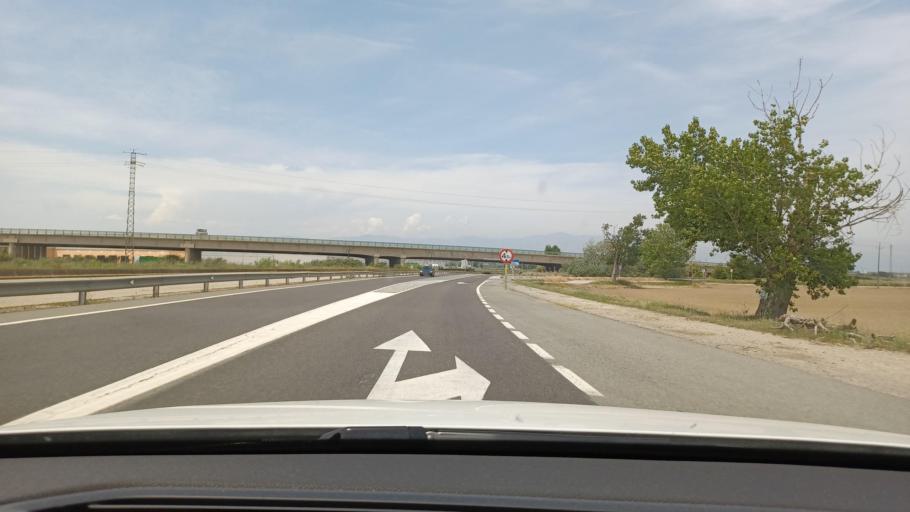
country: ES
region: Catalonia
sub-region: Provincia de Tarragona
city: Amposta
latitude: 40.7135
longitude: 0.5965
